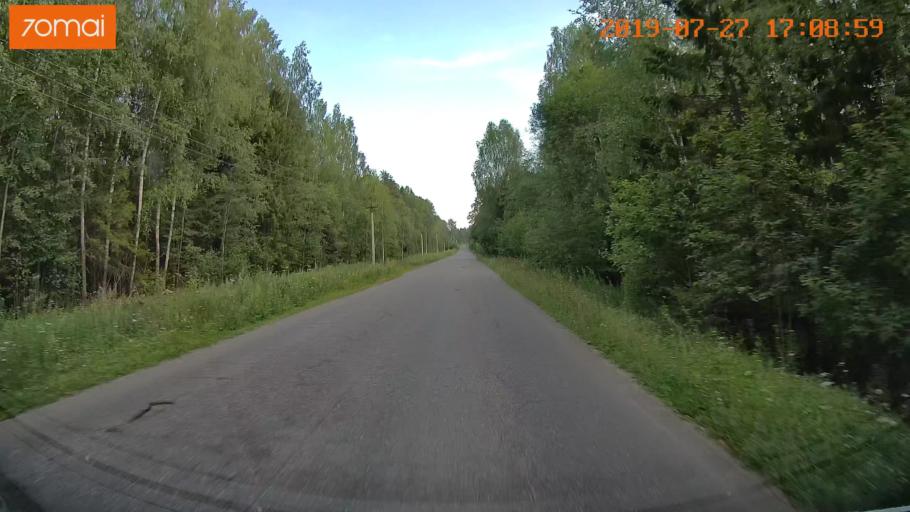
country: RU
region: Ivanovo
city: Novo-Talitsy
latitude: 57.0778
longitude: 40.8442
